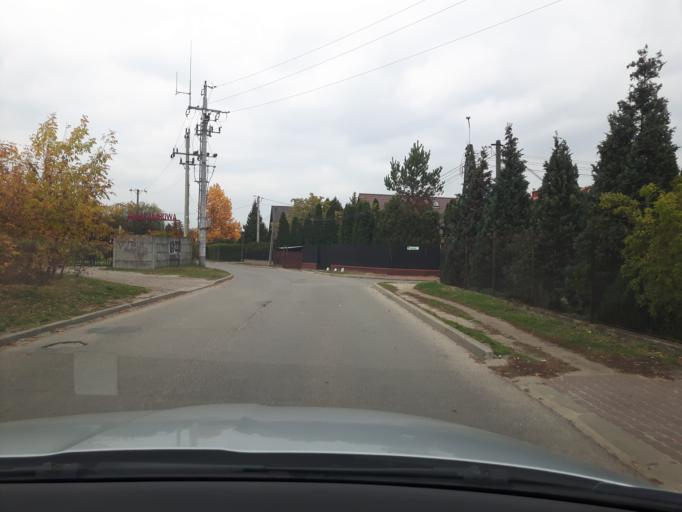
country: PL
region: Masovian Voivodeship
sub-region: Powiat wolominski
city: Zabki
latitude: 52.2885
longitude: 21.0947
